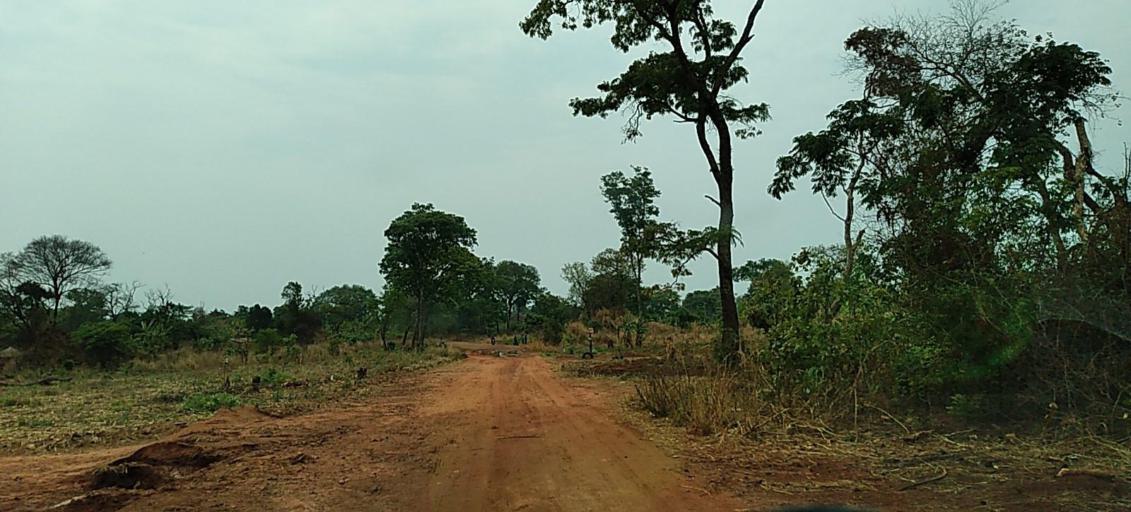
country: ZM
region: North-Western
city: Solwezi
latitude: -12.3390
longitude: 26.5250
